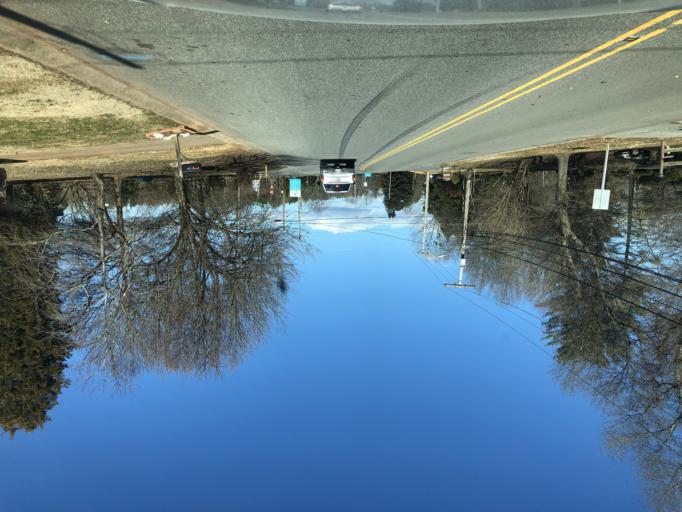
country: US
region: North Carolina
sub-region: Cleveland County
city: Shelby
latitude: 35.3170
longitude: -81.5377
